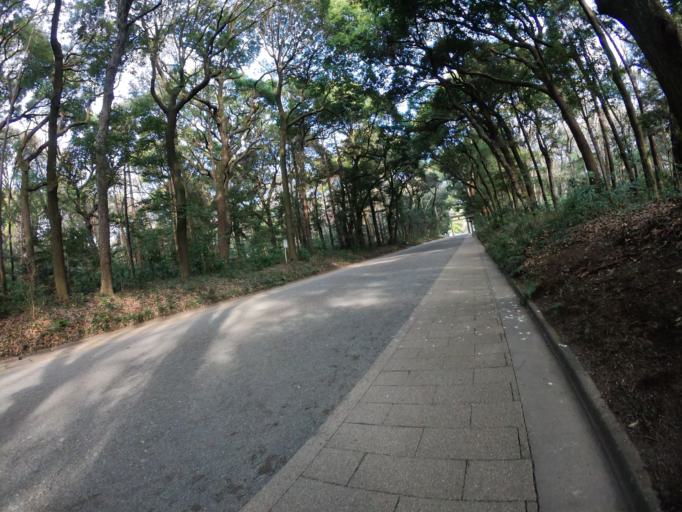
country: JP
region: Chiba
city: Ichihara
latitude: 35.4598
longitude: 140.0185
